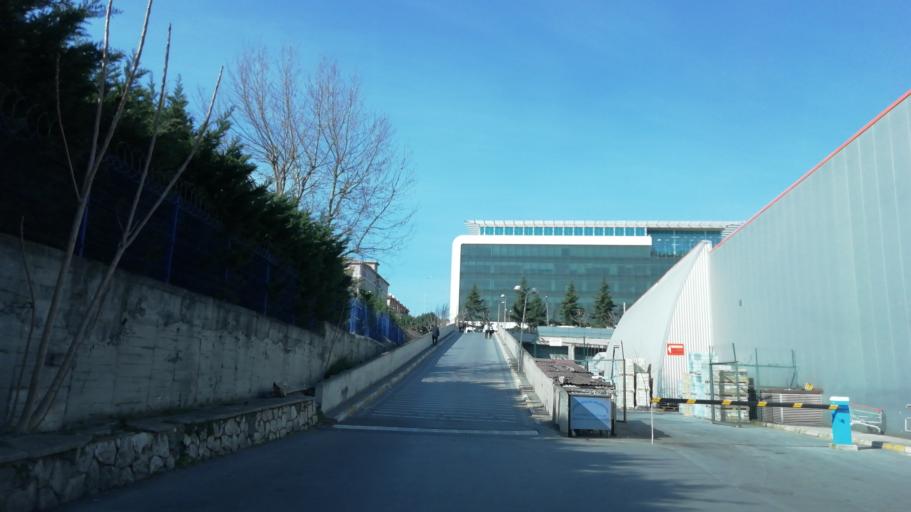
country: TR
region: Istanbul
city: Bahcelievler
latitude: 40.9935
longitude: 28.8327
